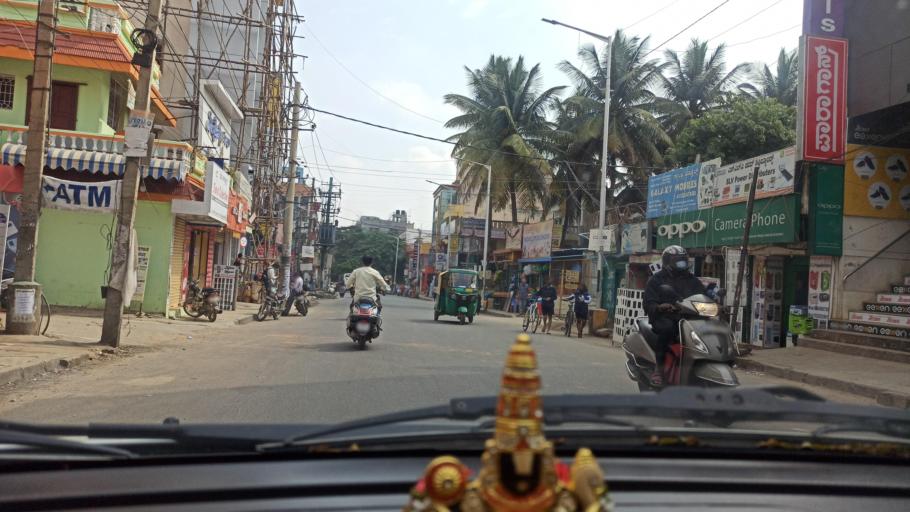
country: IN
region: Karnataka
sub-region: Bangalore Urban
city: Bangalore
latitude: 13.0119
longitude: 77.6692
